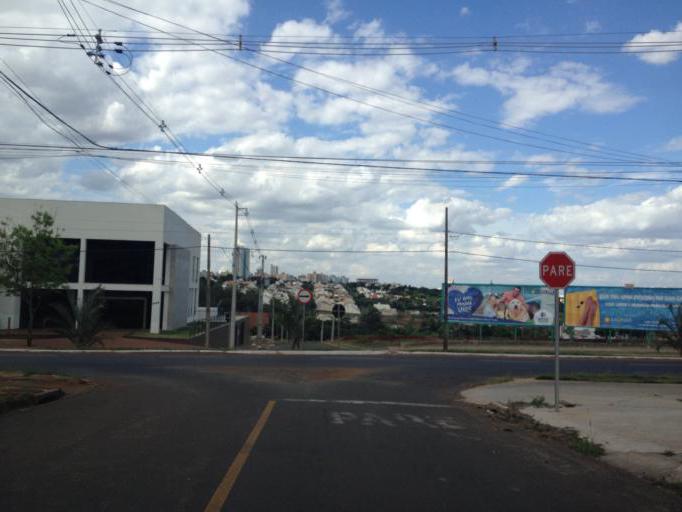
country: BR
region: Parana
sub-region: Maringa
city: Maringa
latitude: -23.4462
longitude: -51.9448
